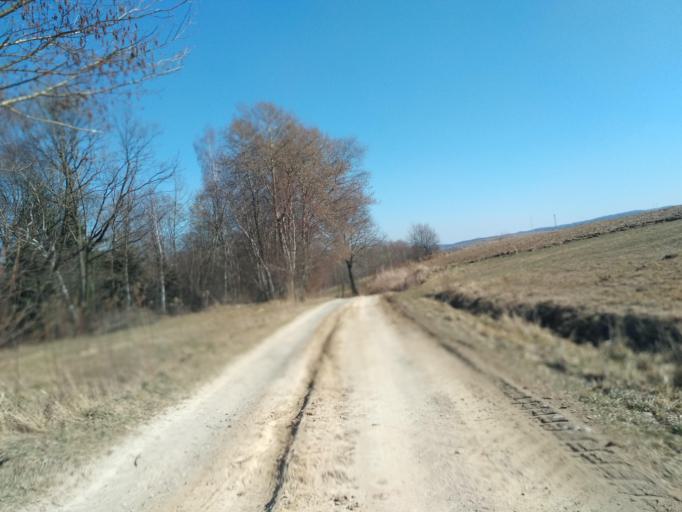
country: PL
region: Subcarpathian Voivodeship
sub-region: Powiat ropczycko-sedziszowski
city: Wielopole Skrzynskie
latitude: 49.9502
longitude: 21.5754
